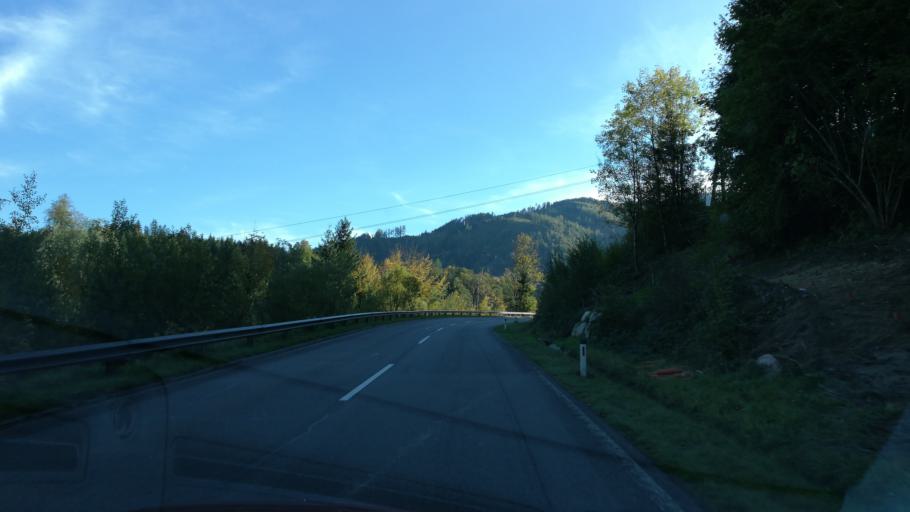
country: AT
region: Styria
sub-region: Politischer Bezirk Liezen
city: Altenmarkt bei Sankt Gallen
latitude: 47.7210
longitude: 14.6670
